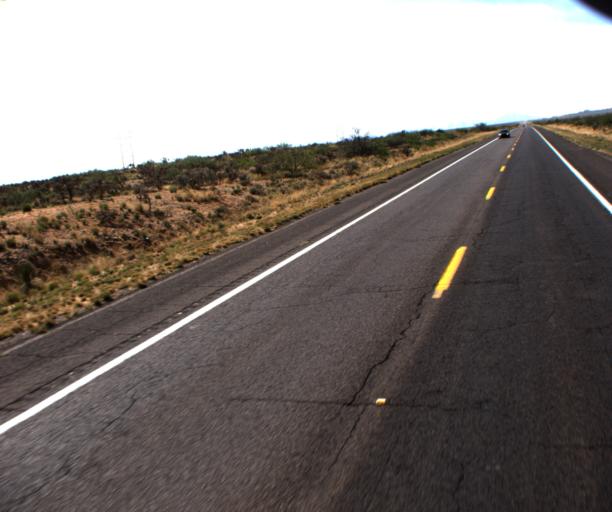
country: US
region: Arizona
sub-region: Graham County
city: Swift Trail Junction
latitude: 32.6124
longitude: -109.6877
